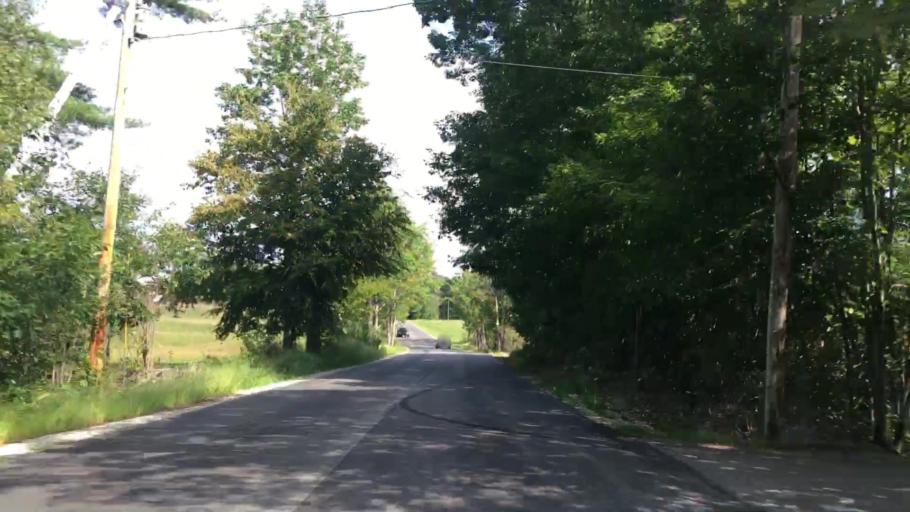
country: US
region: New Hampshire
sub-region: Belknap County
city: Sanbornton
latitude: 43.5060
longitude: -71.6089
